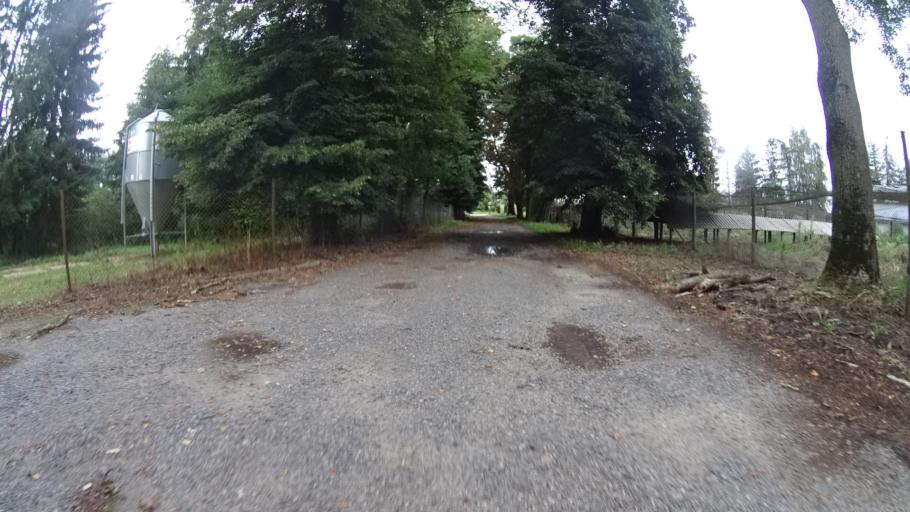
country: PL
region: Masovian Voivodeship
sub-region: Powiat grojecki
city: Goszczyn
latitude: 51.6865
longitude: 20.8594
